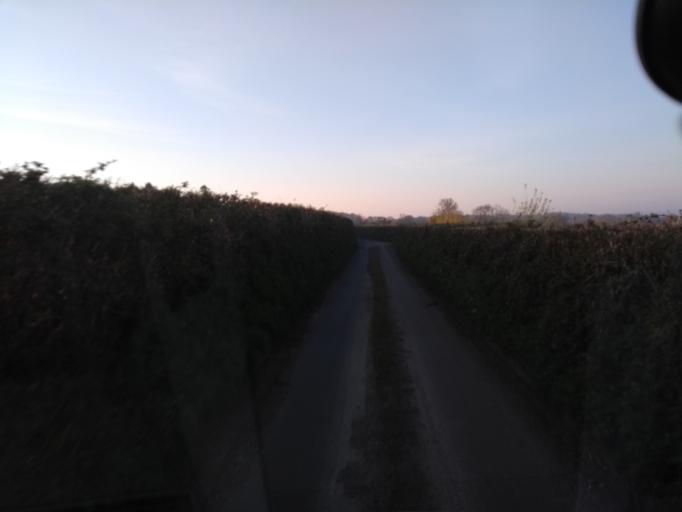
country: GB
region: England
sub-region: Somerset
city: Chard
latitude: 50.8719
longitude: -2.9218
